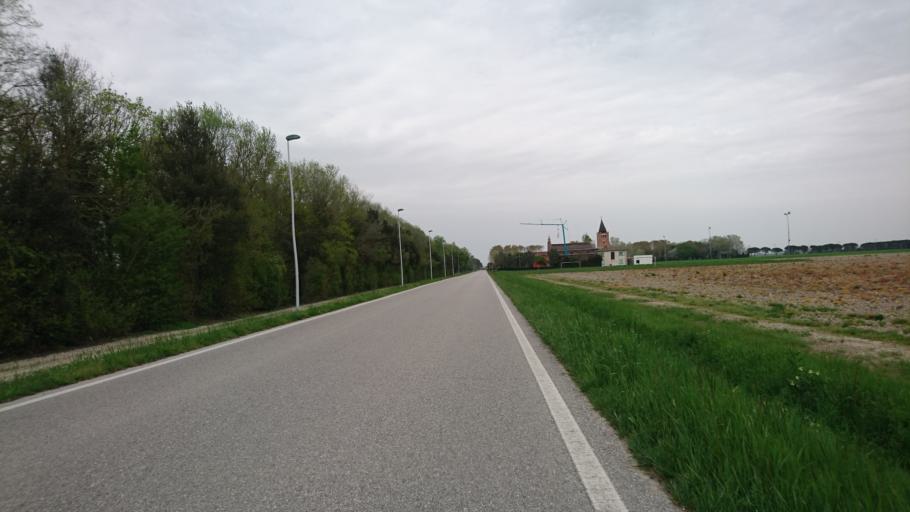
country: IT
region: Veneto
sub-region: Provincia di Venezia
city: Lugugnana
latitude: 45.6524
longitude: 12.9472
